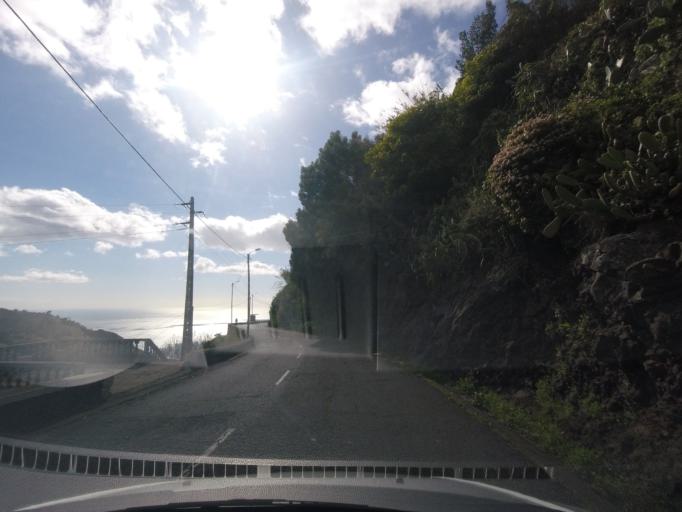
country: PT
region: Madeira
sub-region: Ribeira Brava
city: Campanario
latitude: 32.6638
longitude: -17.0108
